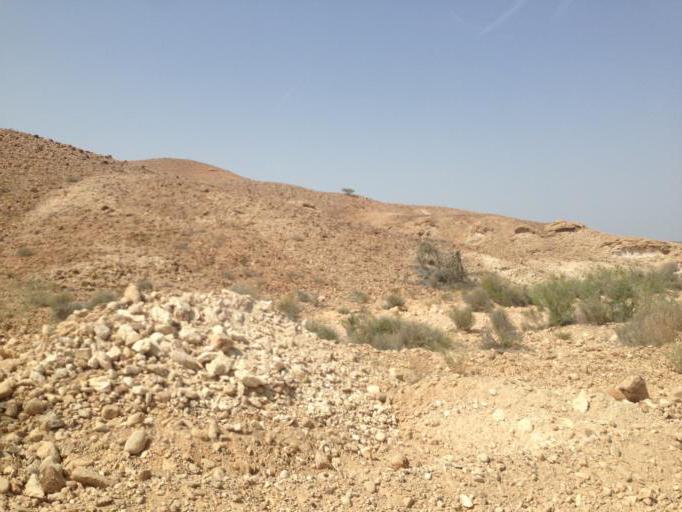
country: OM
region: Ash Sharqiyah
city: Ibra'
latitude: 23.0797
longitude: 58.9031
